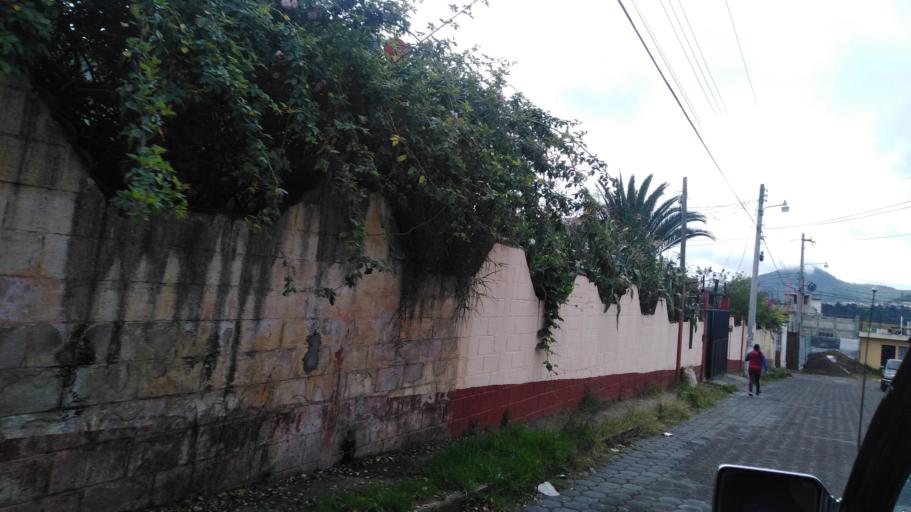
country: GT
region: Quetzaltenango
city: Quetzaltenango
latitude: 14.8536
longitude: -91.5066
